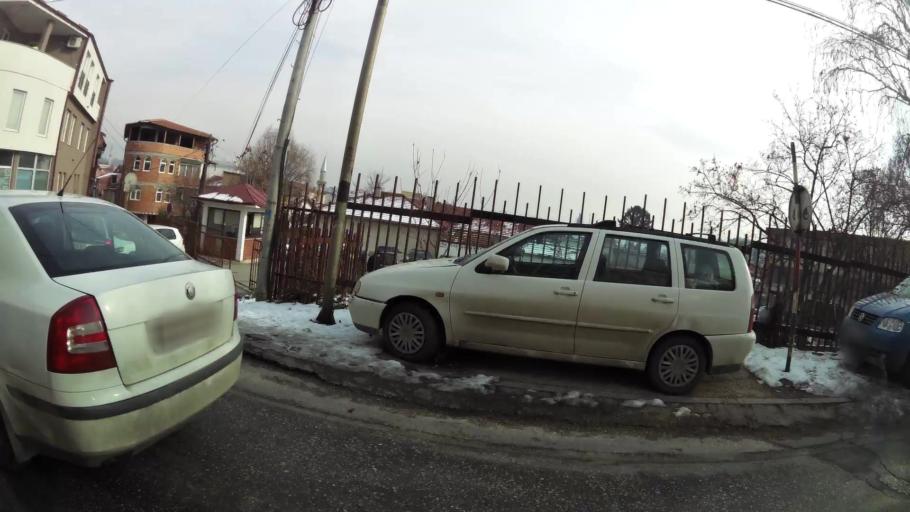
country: MK
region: Karpos
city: Skopje
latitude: 42.0034
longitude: 21.4359
